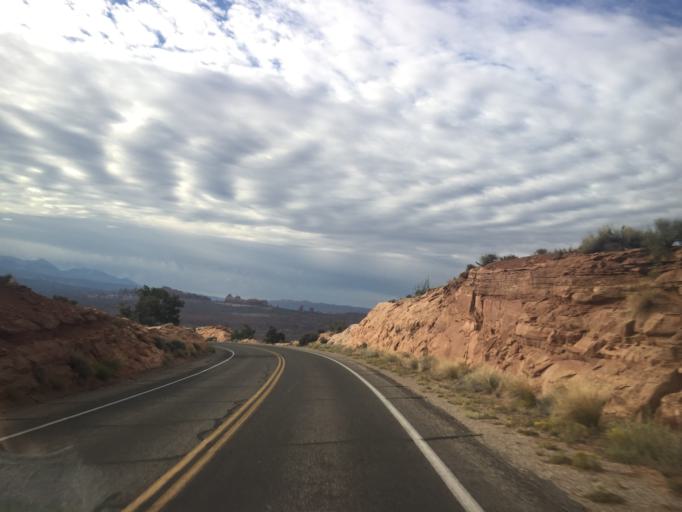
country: US
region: Utah
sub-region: Grand County
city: Moab
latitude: 38.7585
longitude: -109.5834
